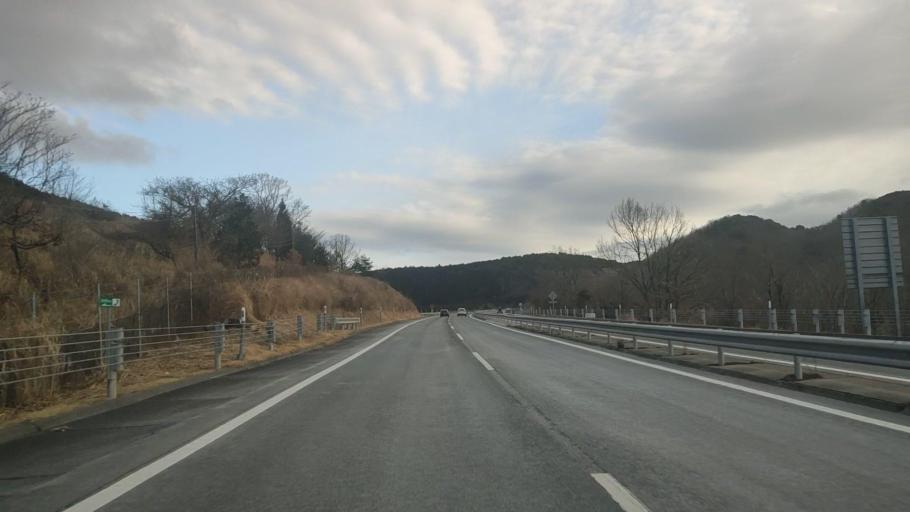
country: JP
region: Oita
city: Beppu
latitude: 33.2901
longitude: 131.3516
